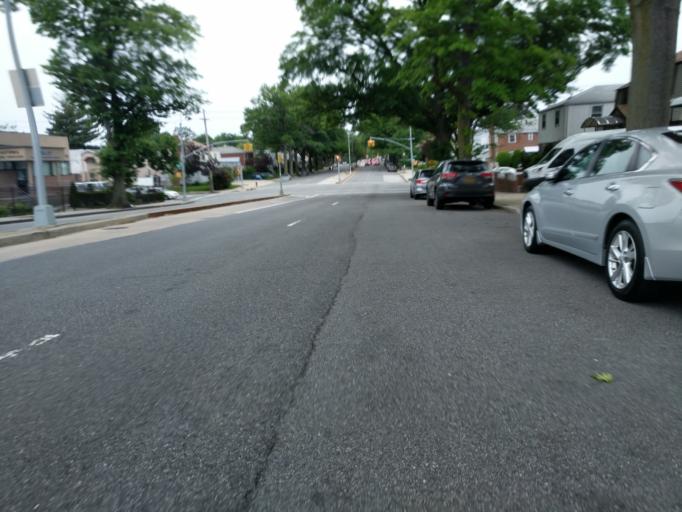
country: US
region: New York
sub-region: Nassau County
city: East Atlantic Beach
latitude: 40.7450
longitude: -73.7765
